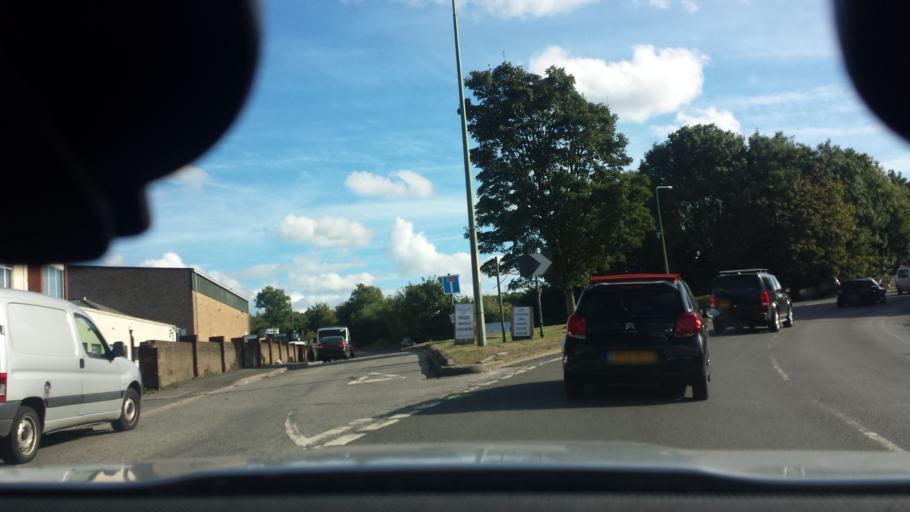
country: GB
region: England
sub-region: Kent
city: Swanley
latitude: 51.3909
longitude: 0.1881
